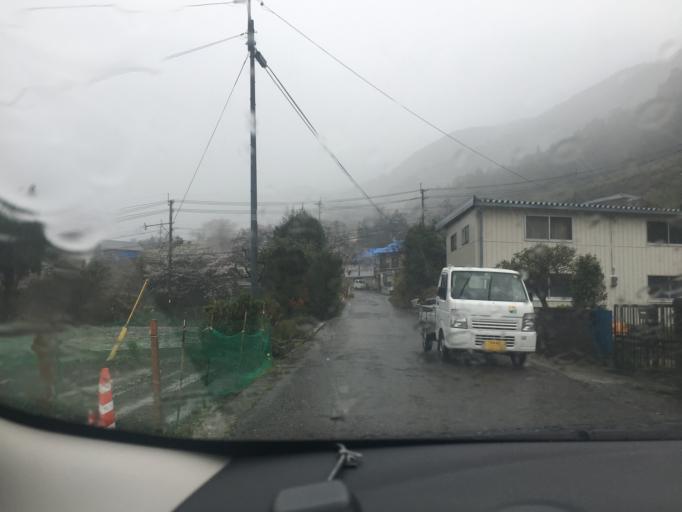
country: JP
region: Kumamoto
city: Ozu
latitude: 32.8791
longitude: 130.9726
